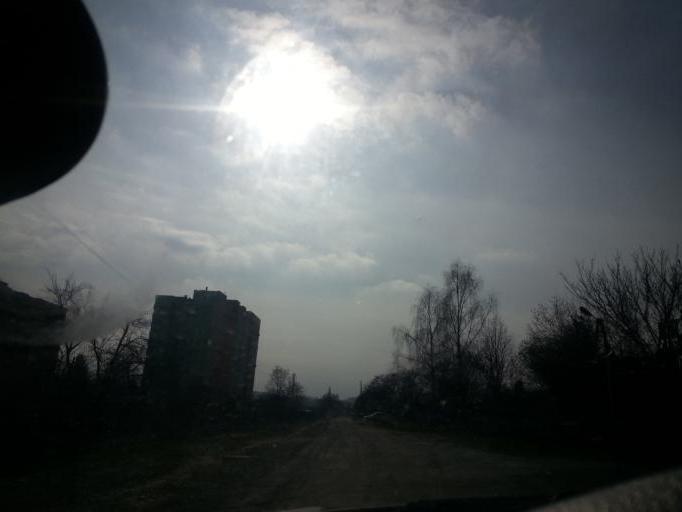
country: PL
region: Lower Silesian Voivodeship
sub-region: Powiat jeleniogorski
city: Jezow Sudecki
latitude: 50.9157
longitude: 15.7427
